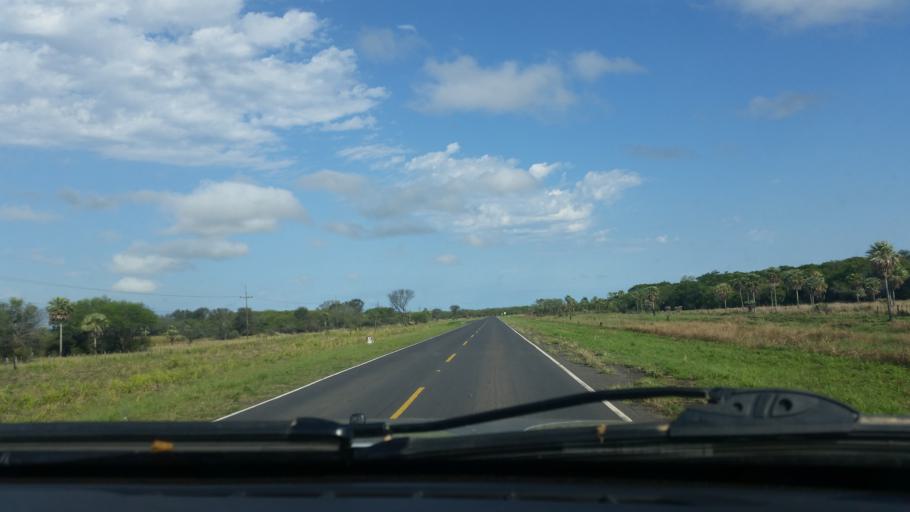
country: PY
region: Presidente Hayes
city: Benjamin Aceval
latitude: -24.9091
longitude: -57.6380
